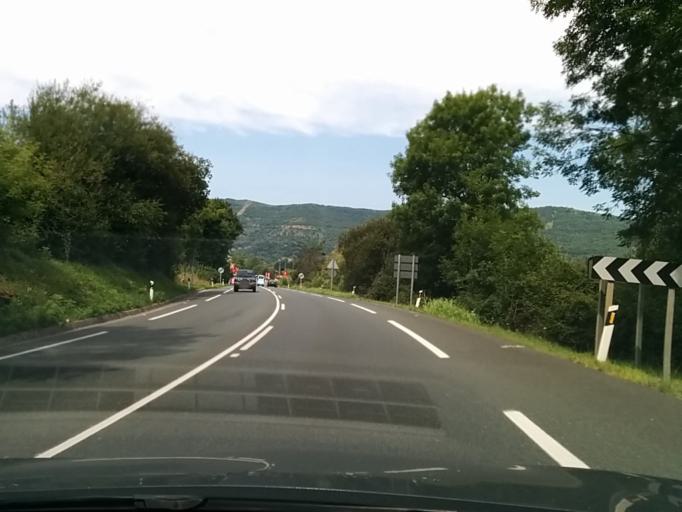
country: ES
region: Basque Country
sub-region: Provincia de Guipuzcoa
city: Irun
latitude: 43.3470
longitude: -1.8038
